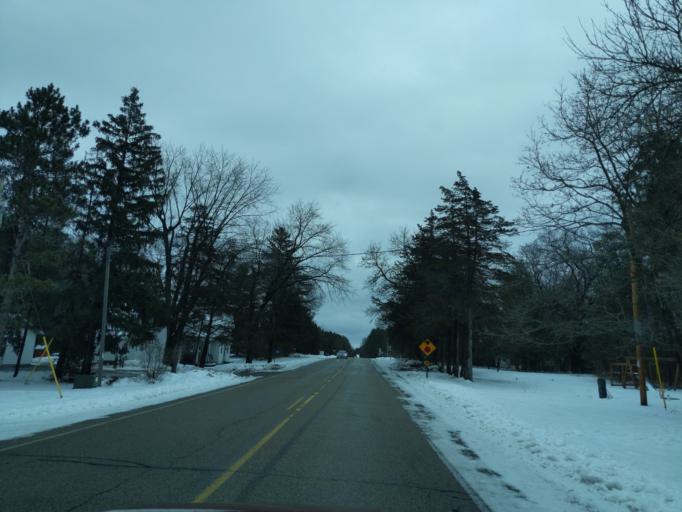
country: US
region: Wisconsin
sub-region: Marquette County
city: Montello
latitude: 43.9197
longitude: -89.3149
